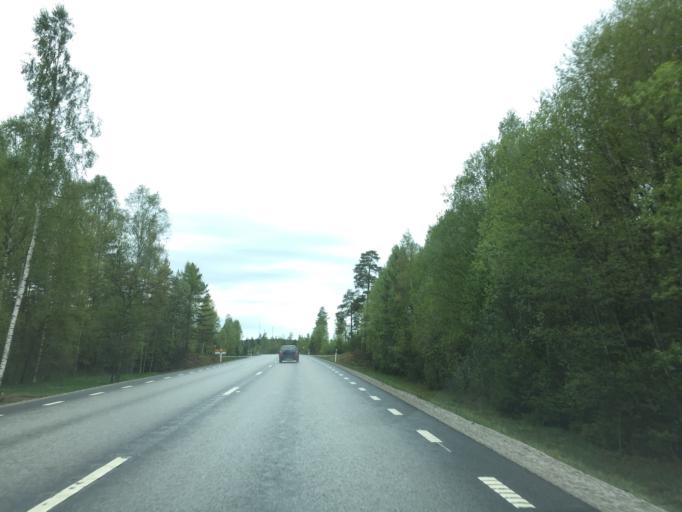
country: SE
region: OErebro
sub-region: Lindesbergs Kommun
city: Lindesberg
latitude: 59.5611
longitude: 15.2194
